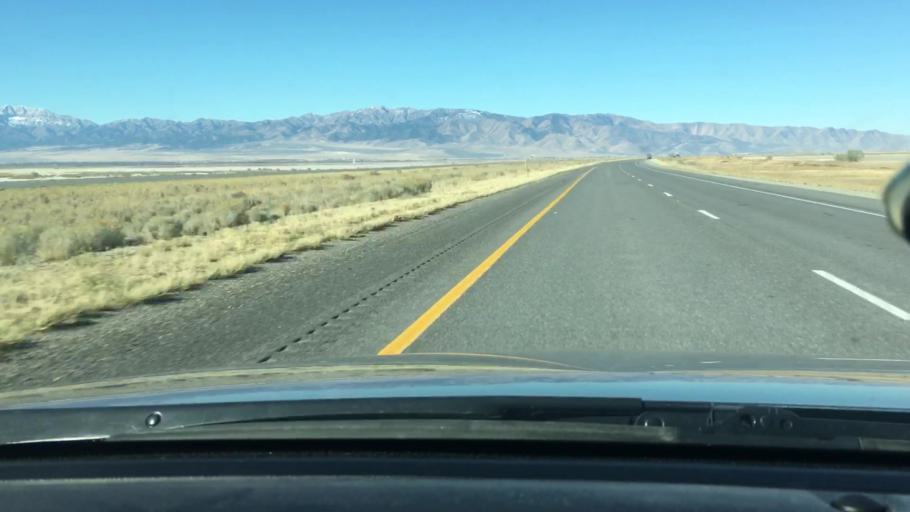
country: US
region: Utah
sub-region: Tooele County
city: Stansbury park
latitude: 40.6626
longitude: -112.3344
